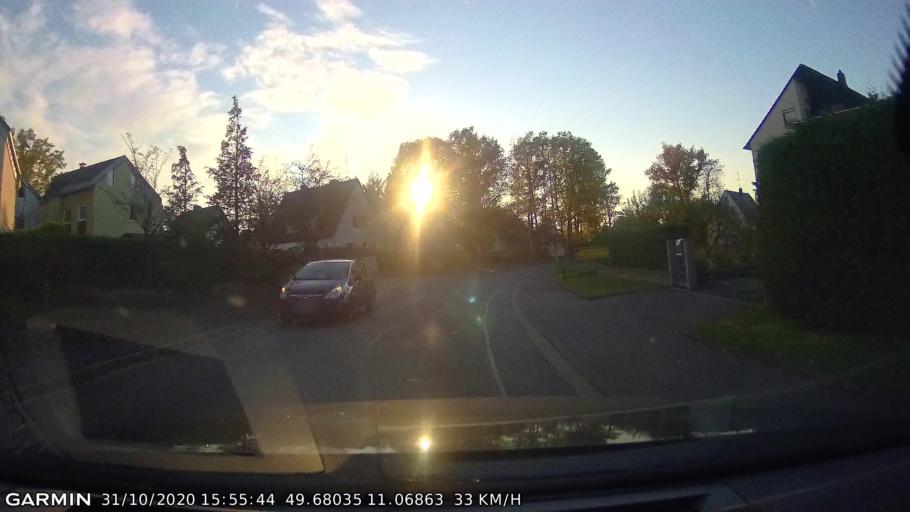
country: DE
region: Bavaria
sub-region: Upper Franconia
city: Poxdorf
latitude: 49.6803
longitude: 11.0687
